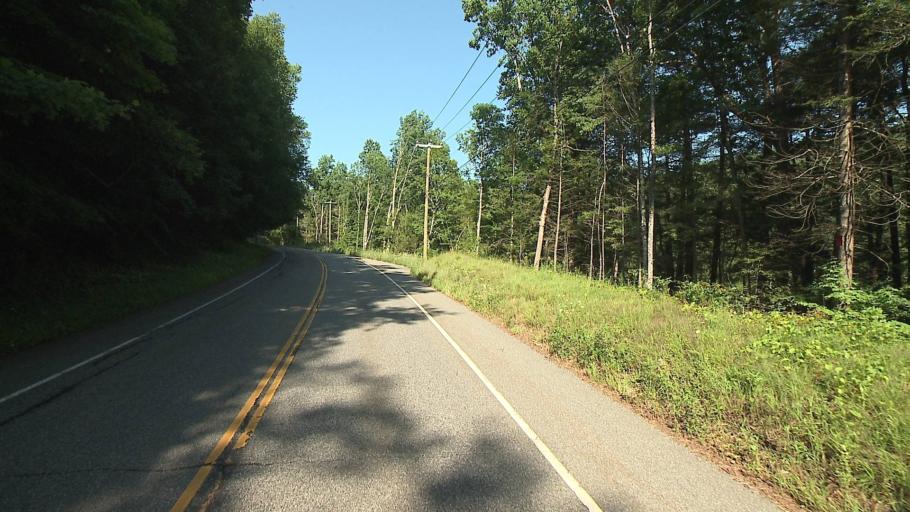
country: US
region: Connecticut
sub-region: Litchfield County
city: Kent
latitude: 41.8231
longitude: -73.3878
